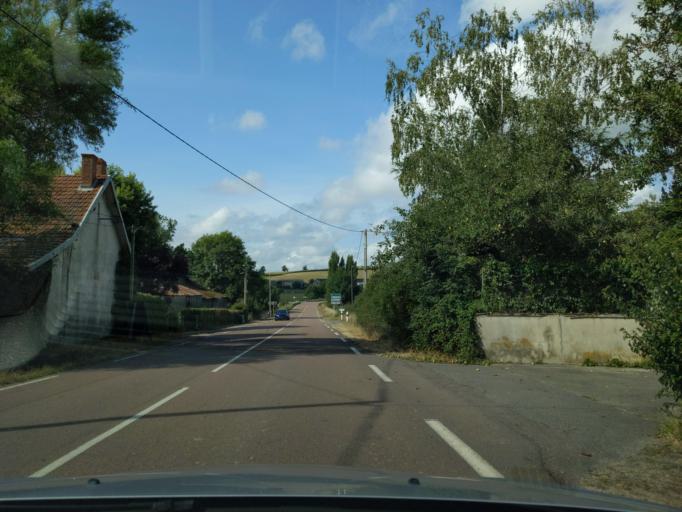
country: FR
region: Bourgogne
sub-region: Departement de Saone-et-Loire
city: Etang-sur-Arroux
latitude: 46.8610
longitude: 4.1042
